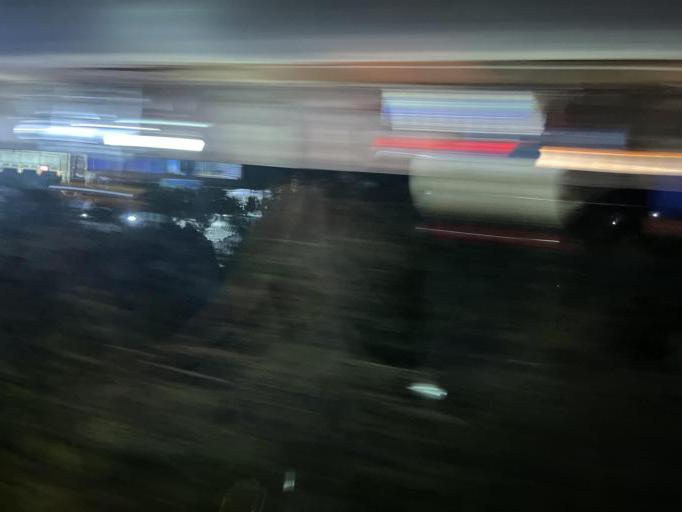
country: IN
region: Odisha
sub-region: Cuttack
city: Cuttack
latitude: 20.3813
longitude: 85.8889
